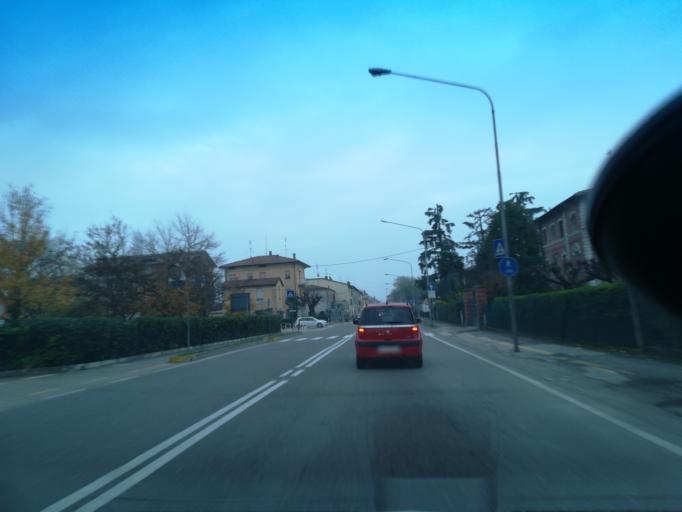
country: IT
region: Emilia-Romagna
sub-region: Provincia di Ravenna
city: Castel Bolognese
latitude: 44.3220
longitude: 11.7936
